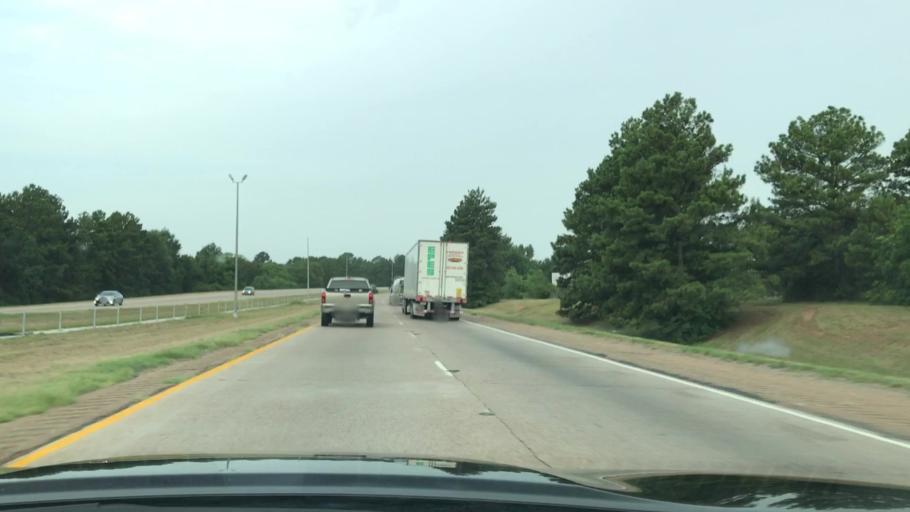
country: US
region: Louisiana
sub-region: Bossier Parish
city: Bossier City
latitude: 32.4170
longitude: -93.7824
